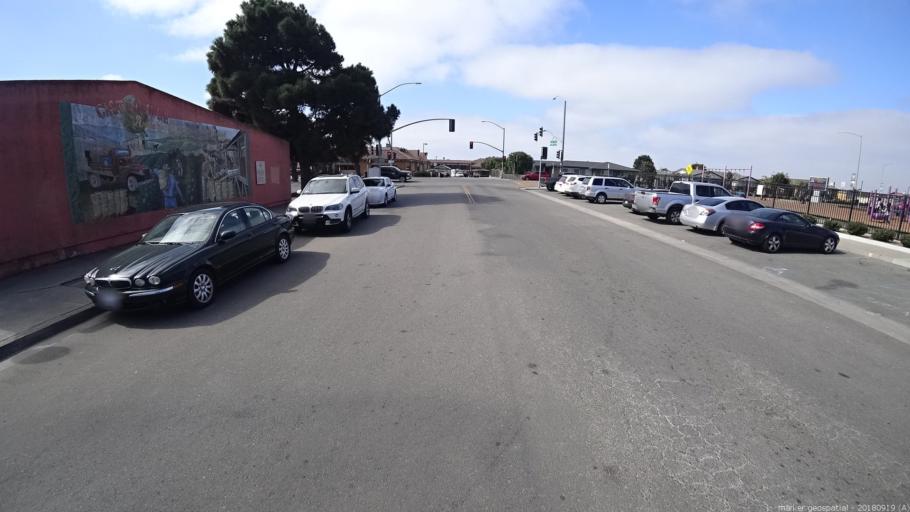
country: US
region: California
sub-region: Monterey County
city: Castroville
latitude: 36.7629
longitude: -121.7534
